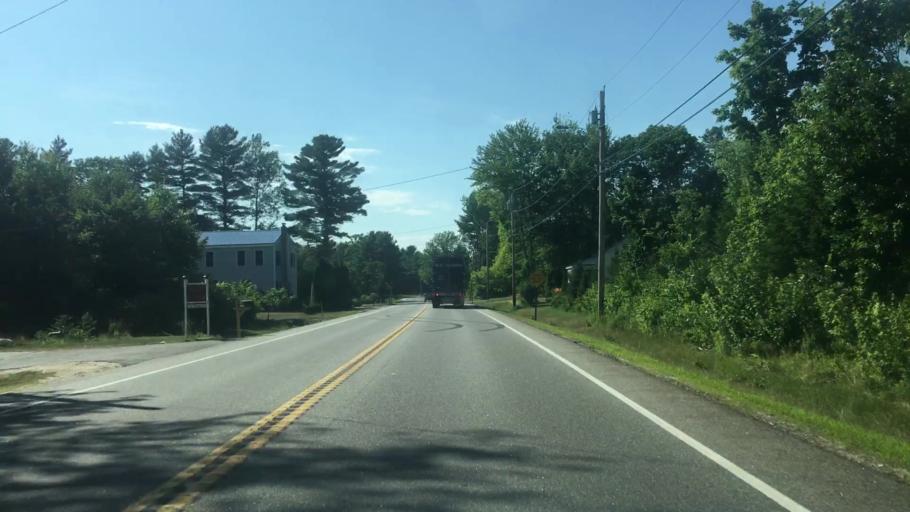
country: US
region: Maine
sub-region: York County
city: Buxton
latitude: 43.5694
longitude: -70.5085
